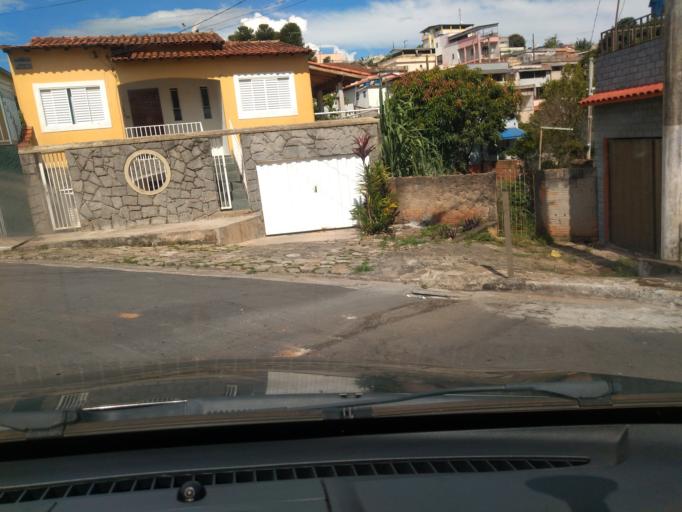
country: BR
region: Minas Gerais
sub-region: Tres Coracoes
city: Tres Coracoes
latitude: -21.6936
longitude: -45.2430
